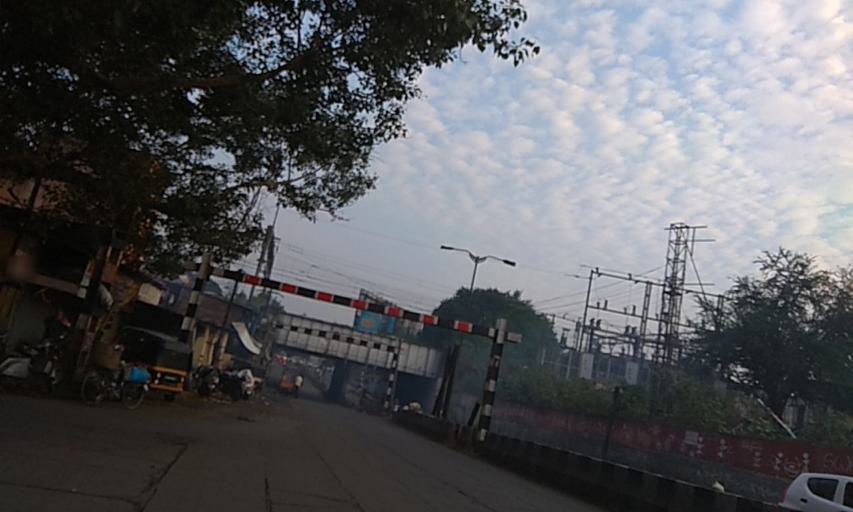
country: IN
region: Maharashtra
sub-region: Pune Division
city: Shivaji Nagar
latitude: 18.5280
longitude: 73.8633
